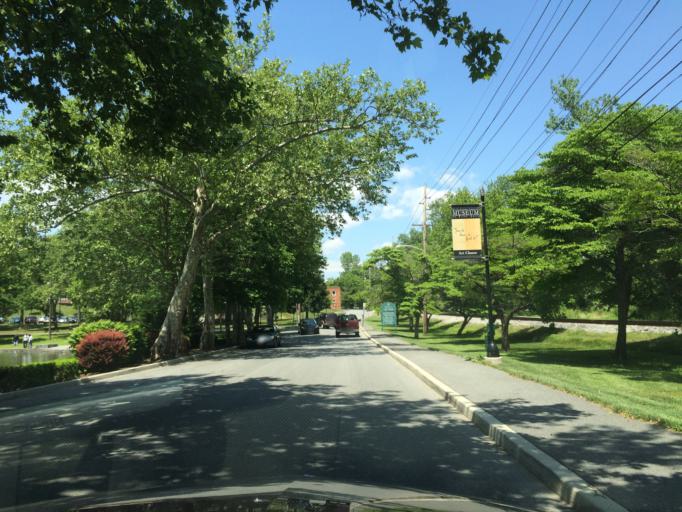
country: US
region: Maryland
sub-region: Washington County
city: Hagerstown
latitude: 39.6381
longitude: -77.7293
